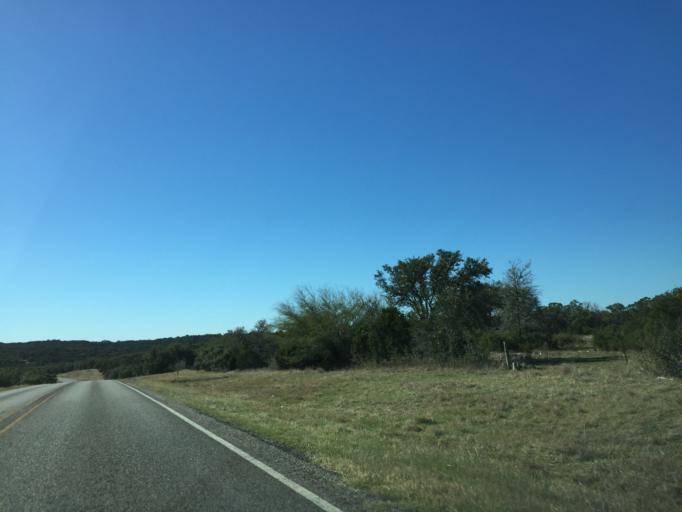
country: US
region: Texas
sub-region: Comal County
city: Garden Ridge
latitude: 29.7250
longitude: -98.3090
